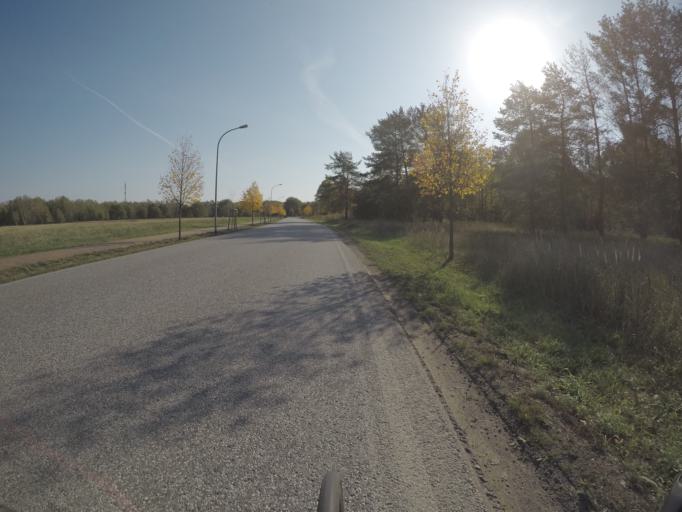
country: DE
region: Brandenburg
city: Leegebruch
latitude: 52.7258
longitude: 13.2239
